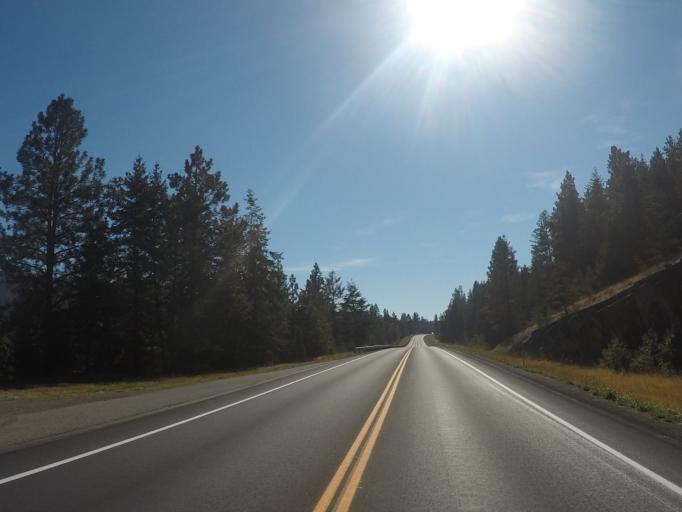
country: US
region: Montana
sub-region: Lake County
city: Polson
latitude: 47.8039
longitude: -114.2372
